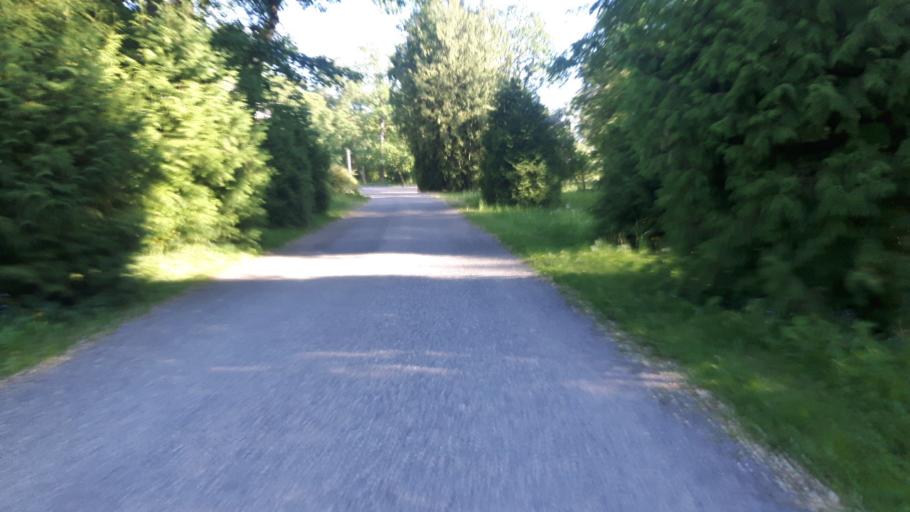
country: EE
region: Raplamaa
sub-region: Kehtna vald
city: Kehtna
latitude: 58.9235
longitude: 24.8727
